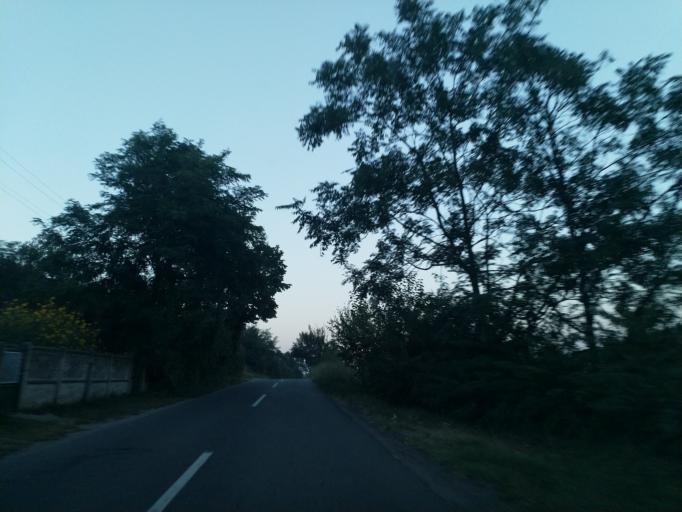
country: RS
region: Central Serbia
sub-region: Rasinski Okrug
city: Krusevac
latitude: 43.6434
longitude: 21.3737
